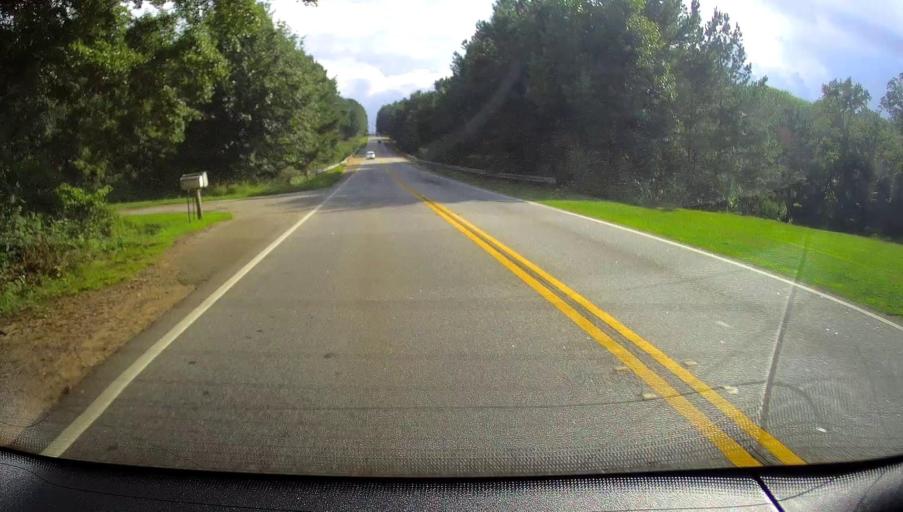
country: US
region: Georgia
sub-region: Coweta County
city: Senoia
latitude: 33.3063
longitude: -84.5333
